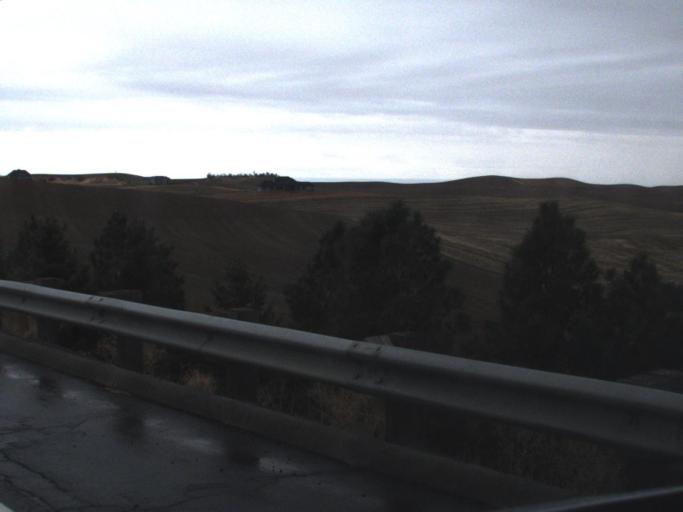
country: US
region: Washington
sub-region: Whitman County
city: Pullman
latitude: 46.7173
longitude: -117.2194
